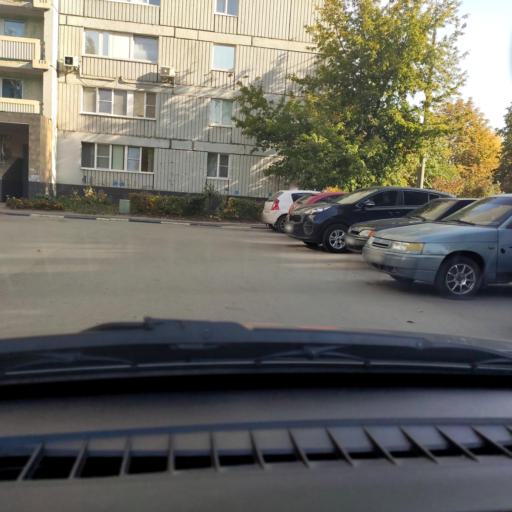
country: RU
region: Samara
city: Tol'yatti
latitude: 53.5256
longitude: 49.3088
